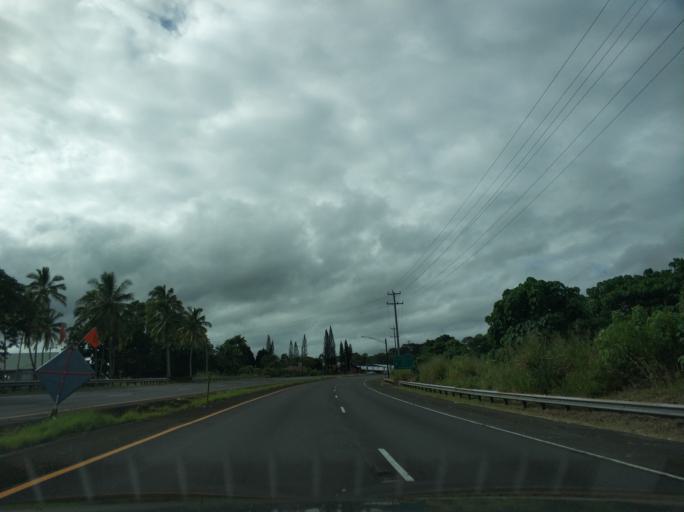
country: US
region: Hawaii
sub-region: Hawaii County
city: Kea'au
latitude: 19.6261
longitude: -155.0399
